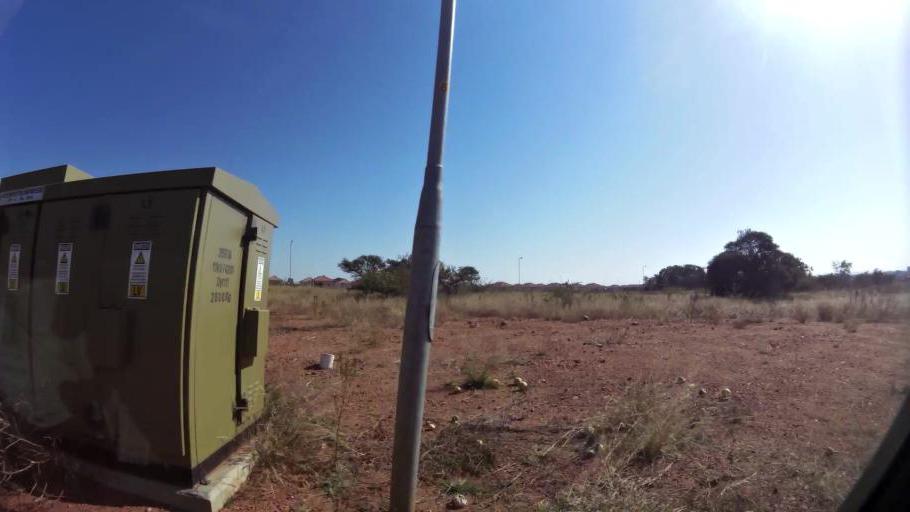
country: ZA
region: North-West
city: Ga-Rankuwa
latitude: -25.6433
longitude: 28.0796
